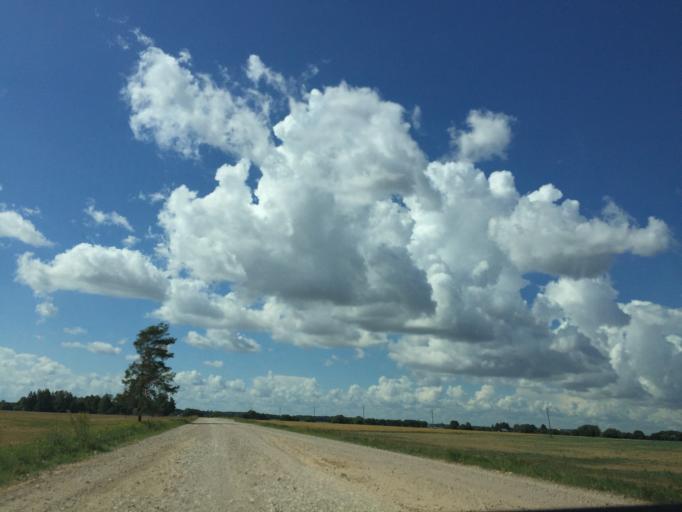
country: LV
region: Rundales
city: Pilsrundale
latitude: 56.3877
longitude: 24.0902
